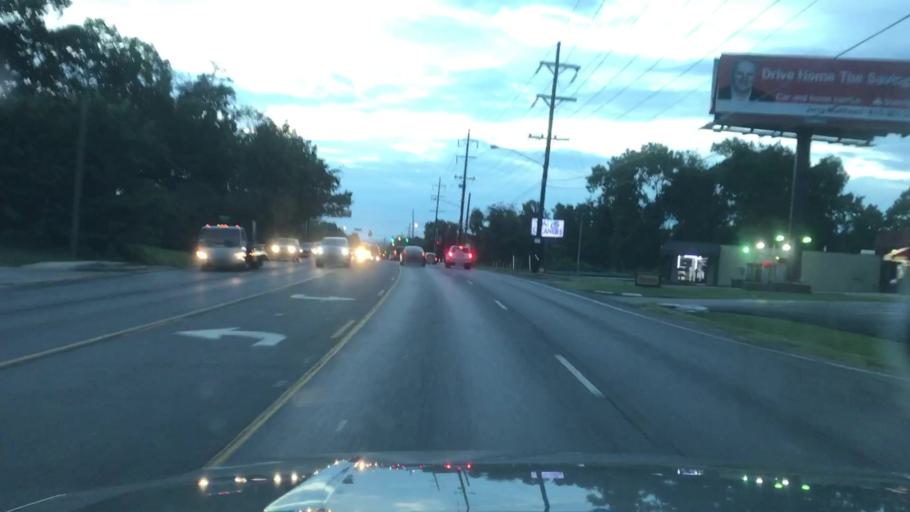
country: US
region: Tennessee
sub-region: Rutherford County
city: La Vergne
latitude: 36.0951
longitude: -86.6541
